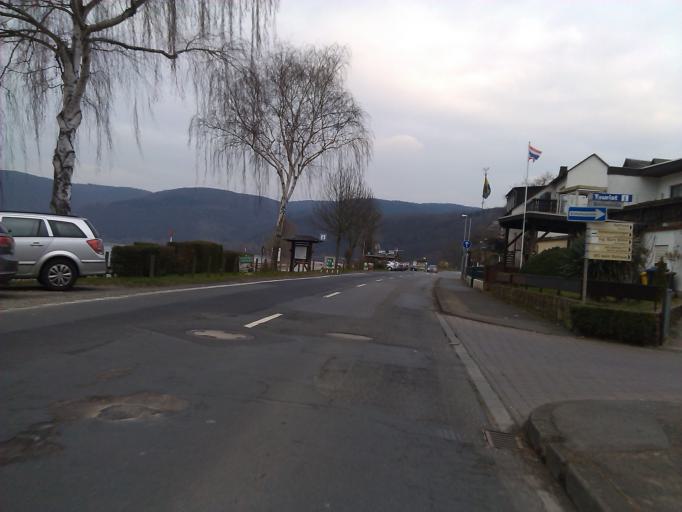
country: DE
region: Rheinland-Pfalz
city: Osterspai
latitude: 50.2459
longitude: 7.6187
